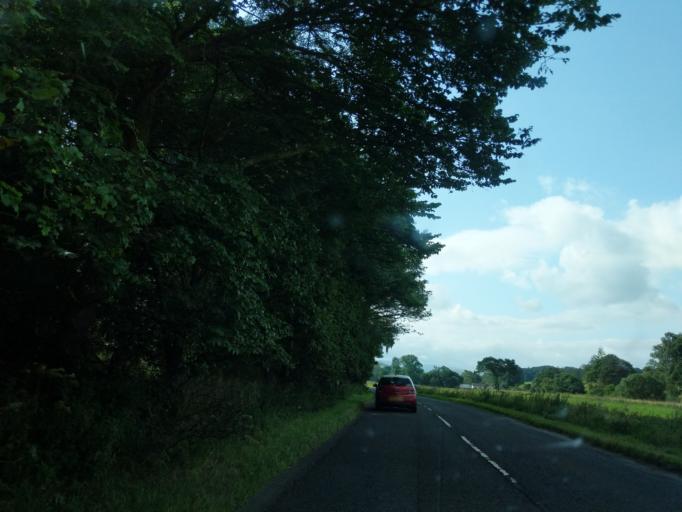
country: GB
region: Scotland
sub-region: The Scottish Borders
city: Peebles
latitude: 55.7315
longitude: -3.2061
